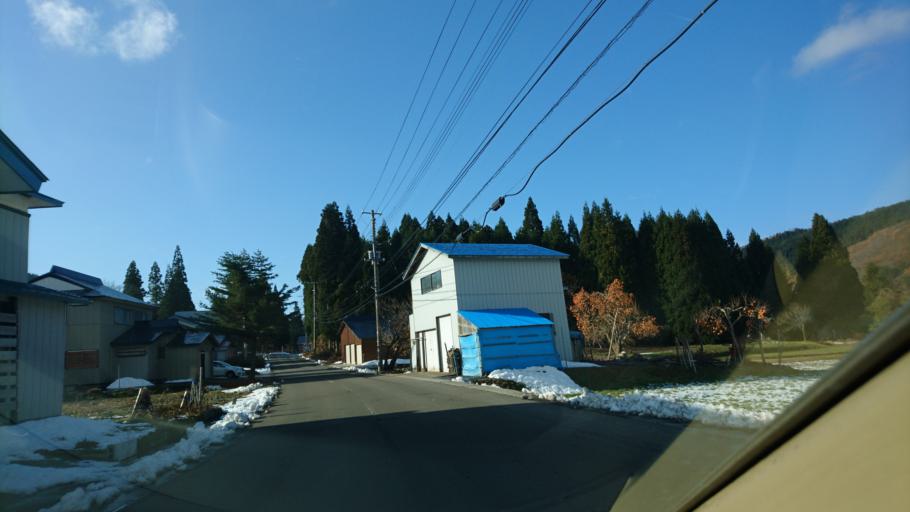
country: JP
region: Iwate
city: Kitakami
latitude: 39.2967
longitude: 140.8348
